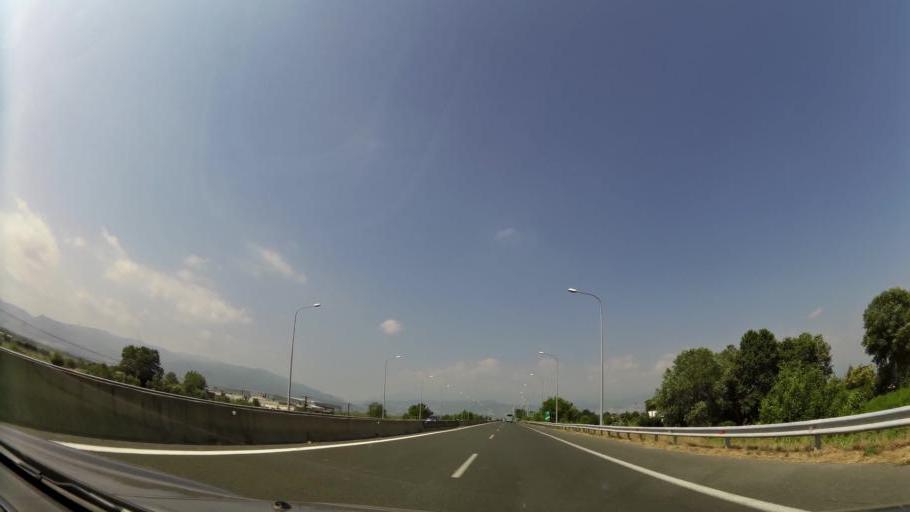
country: GR
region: Central Macedonia
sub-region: Nomos Imathias
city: Kouloura
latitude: 40.5433
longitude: 22.3211
